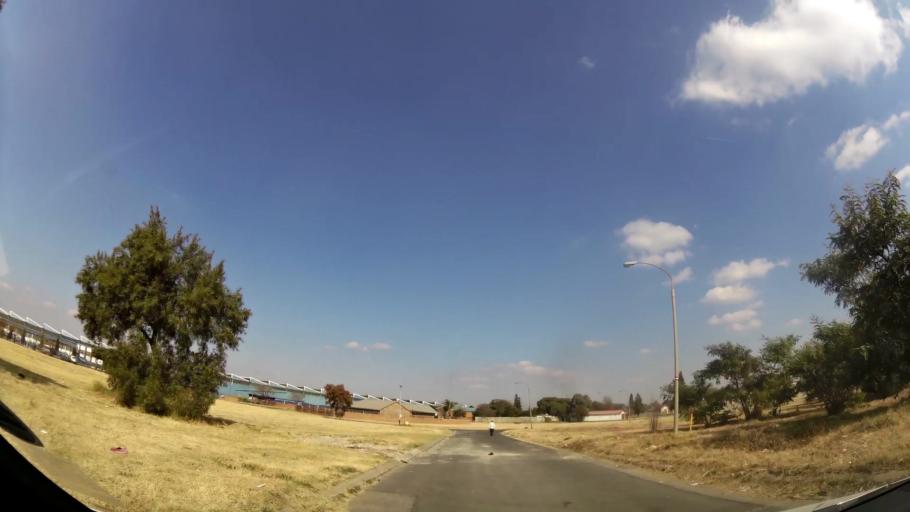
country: ZA
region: Gauteng
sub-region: Ekurhuleni Metropolitan Municipality
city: Boksburg
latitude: -26.1912
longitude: 28.2135
